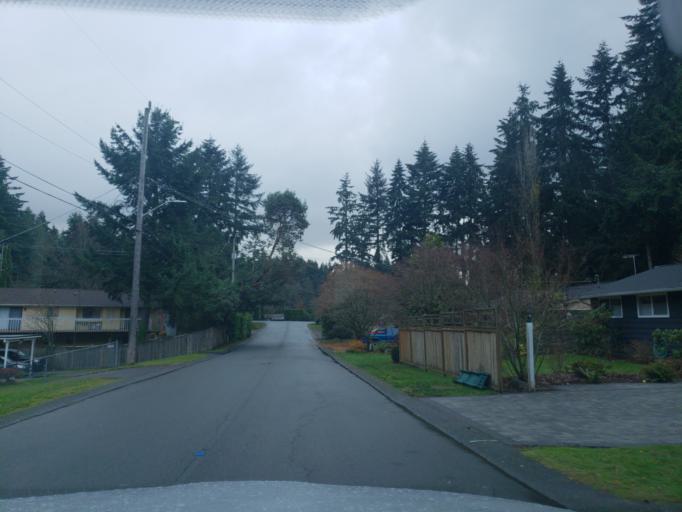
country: US
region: Washington
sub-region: Snohomish County
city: Esperance
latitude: 47.7715
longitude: -122.3580
